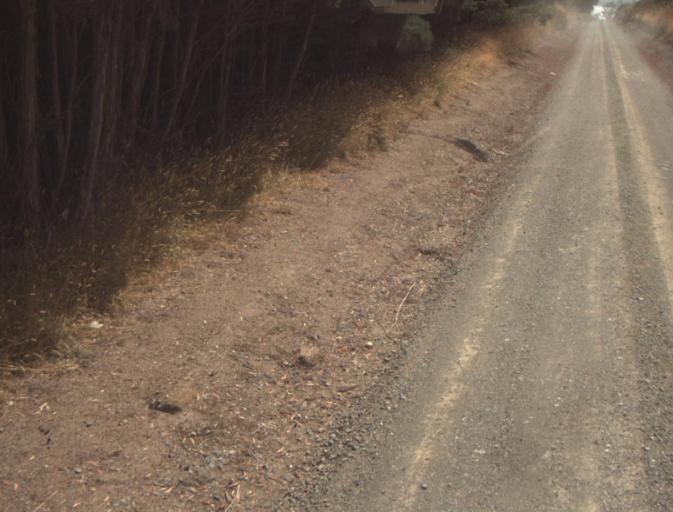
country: AU
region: Tasmania
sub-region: Launceston
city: Mayfield
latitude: -41.1957
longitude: 147.1700
